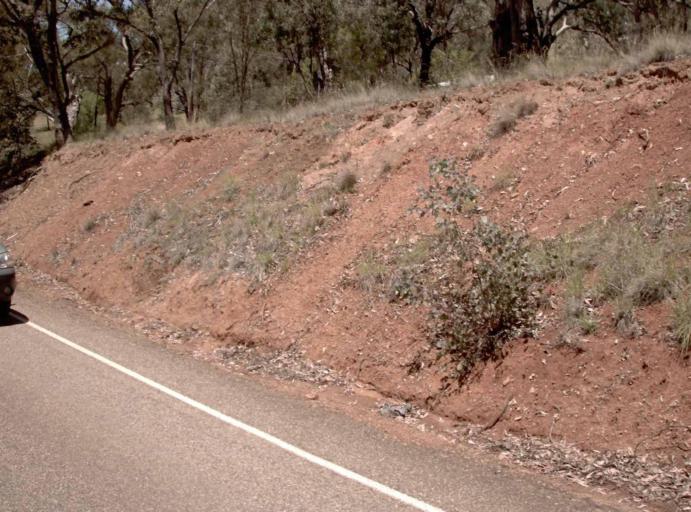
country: AU
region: Victoria
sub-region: East Gippsland
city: Bairnsdale
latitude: -37.3663
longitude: 147.8329
